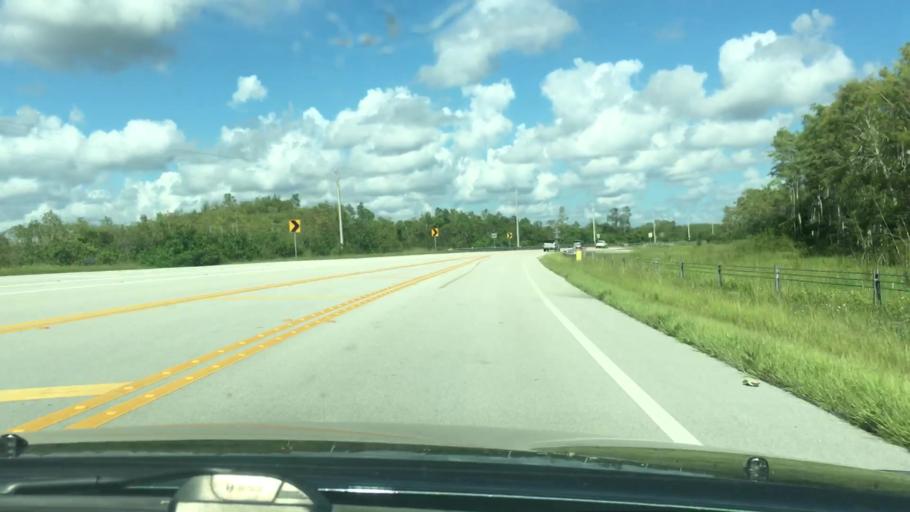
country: US
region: Florida
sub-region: Miami-Dade County
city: Kendall West
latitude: 25.7625
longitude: -80.8284
